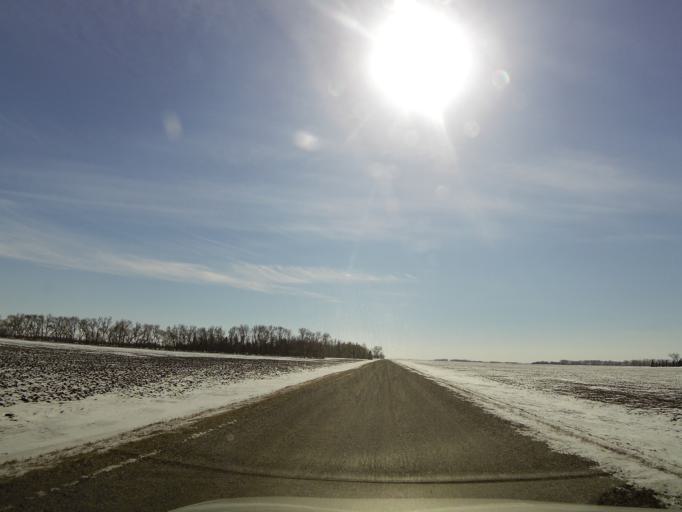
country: US
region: North Dakota
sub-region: Walsh County
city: Grafton
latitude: 48.4107
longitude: -97.2119
